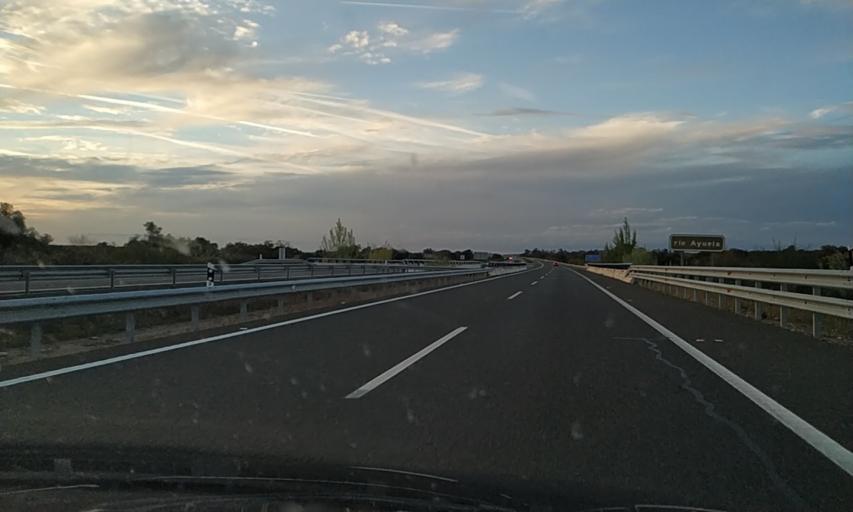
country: ES
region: Extremadura
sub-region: Provincia de Caceres
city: Casas de Don Antonio
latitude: 39.2364
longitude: -6.3033
